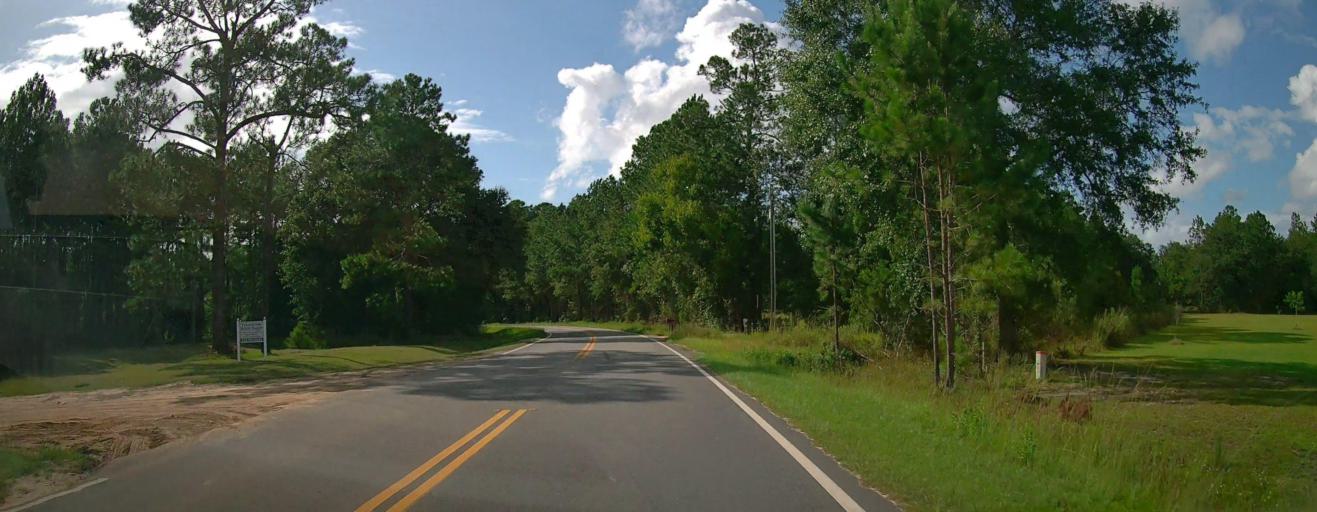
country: US
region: Georgia
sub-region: Coffee County
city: Douglas
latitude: 31.4506
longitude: -82.8803
